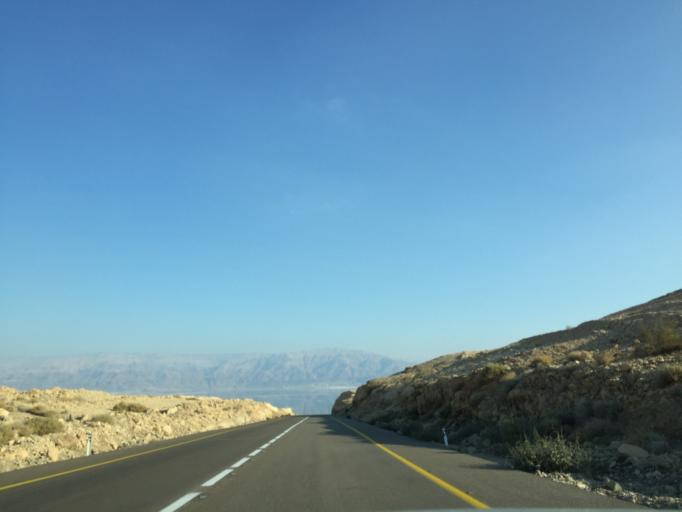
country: IL
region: Southern District
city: `En Boqeq
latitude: 31.1596
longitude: 35.3300
